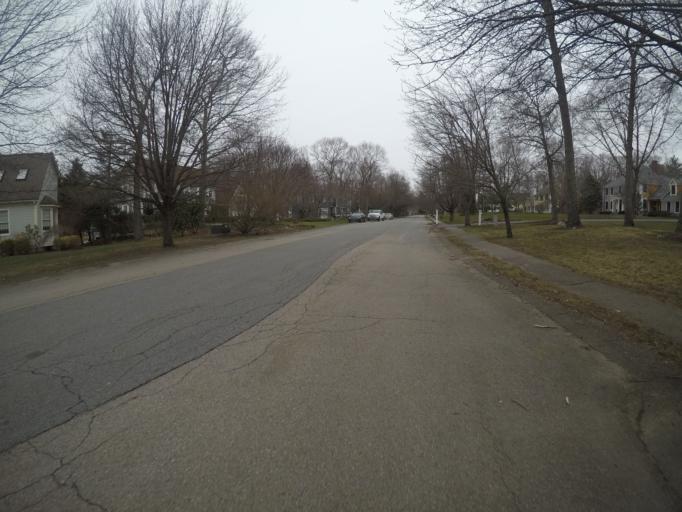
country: US
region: Massachusetts
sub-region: Bristol County
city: Easton
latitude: 42.0532
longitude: -71.1443
